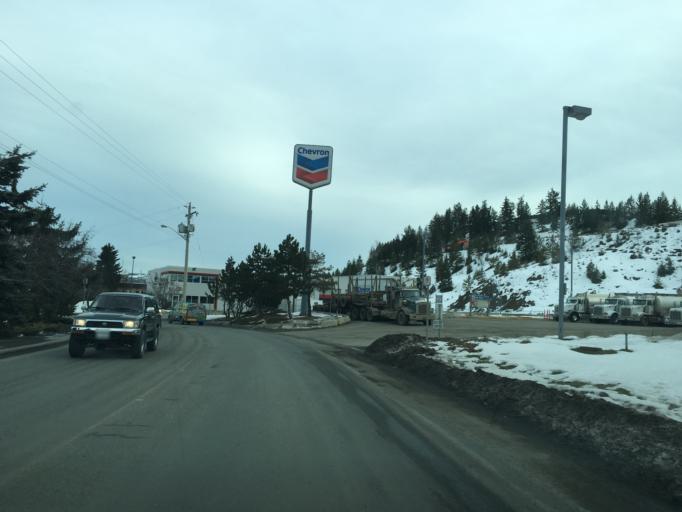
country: CA
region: British Columbia
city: Kamloops
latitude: 50.6592
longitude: -120.3991
